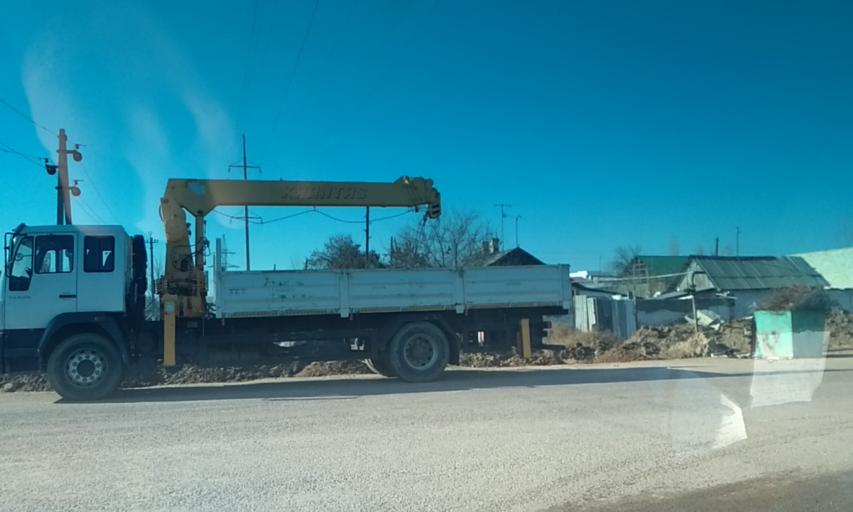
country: UZ
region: Sirdaryo
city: Guliston
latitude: 40.5043
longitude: 68.7712
